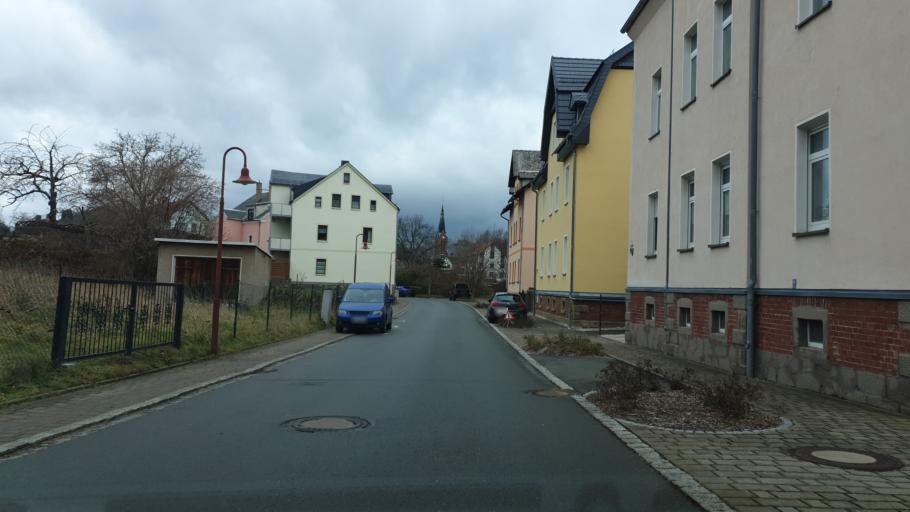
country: DE
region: Saxony
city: Hohndorf
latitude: 50.7421
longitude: 12.6776
